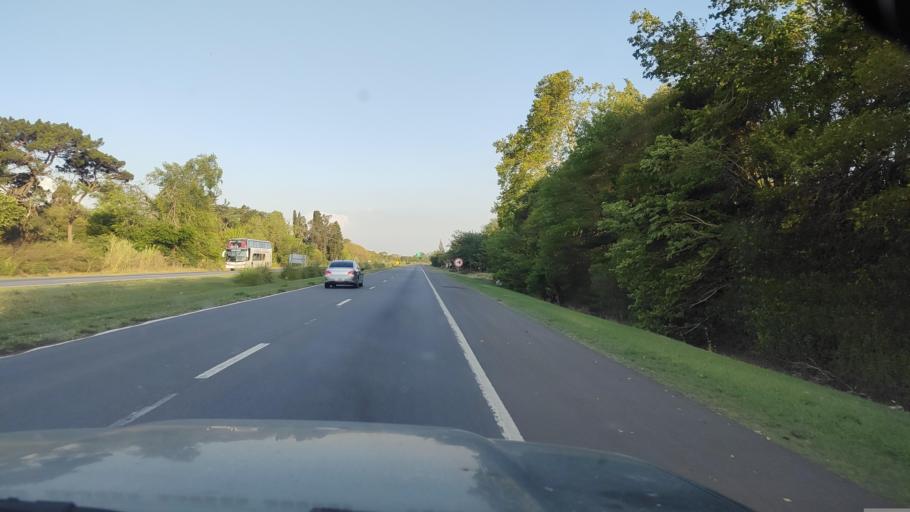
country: AR
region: Buenos Aires
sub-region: Partido de Lujan
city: Lujan
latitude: -34.5467
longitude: -59.2069
